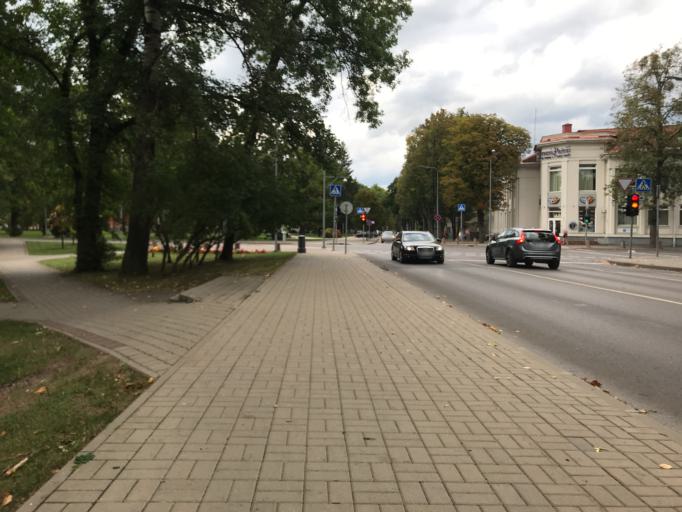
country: LT
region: Alytaus apskritis
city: Druskininkai
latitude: 54.0157
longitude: 23.9754
